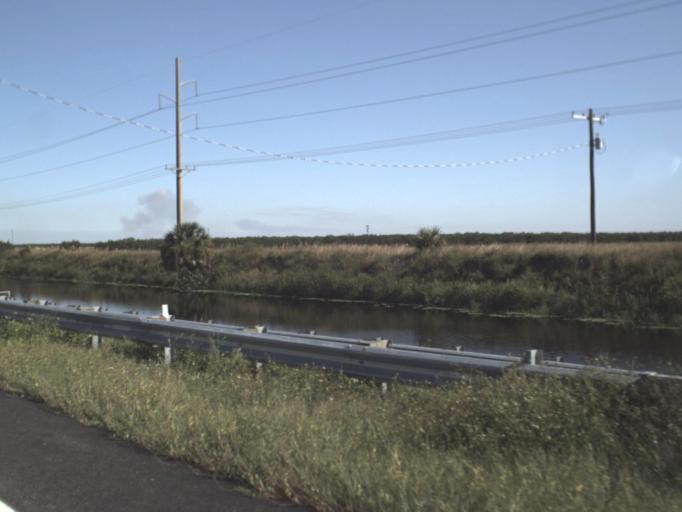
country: US
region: Florida
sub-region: Glades County
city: Moore Haven
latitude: 26.7532
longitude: -81.0935
